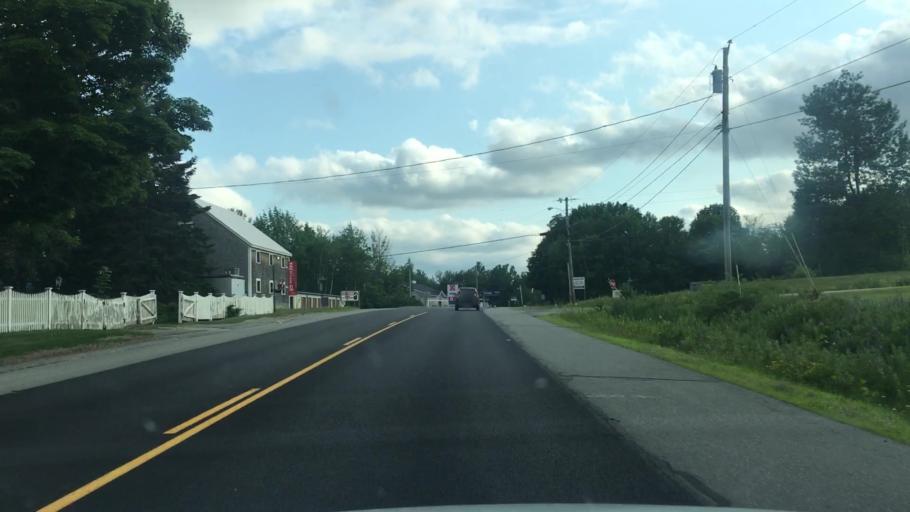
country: US
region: Maine
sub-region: Knox County
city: Washington
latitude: 44.3874
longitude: -69.3580
